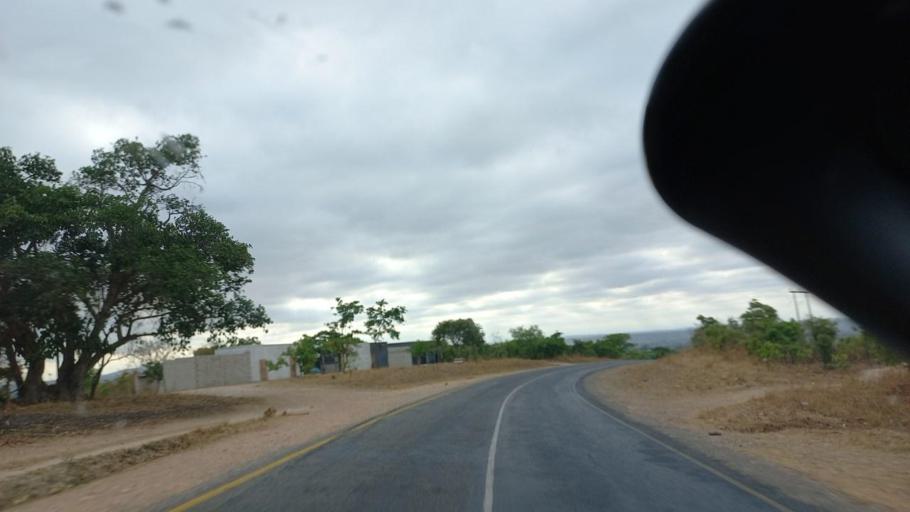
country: ZM
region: Lusaka
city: Chongwe
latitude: -15.2731
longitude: 28.7670
